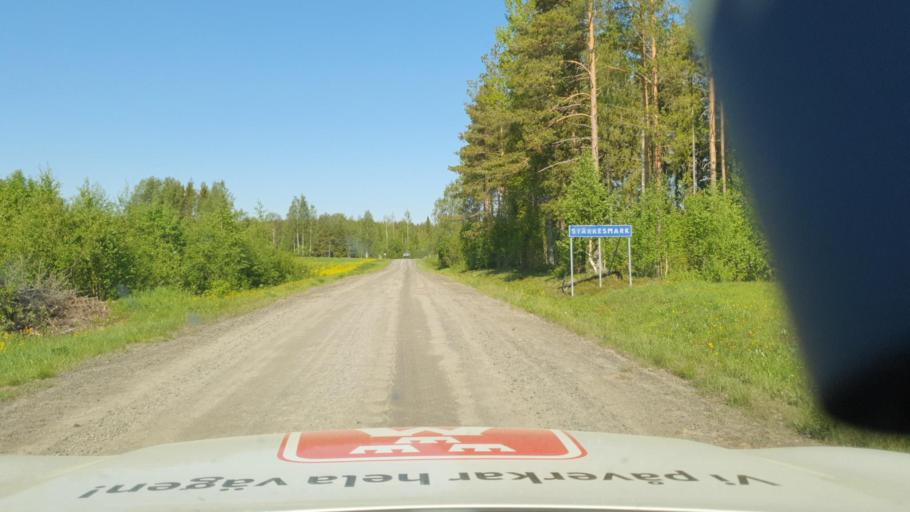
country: SE
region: Vaesterbotten
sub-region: Vannas Kommun
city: Vaennaes
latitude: 64.0207
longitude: 19.7583
